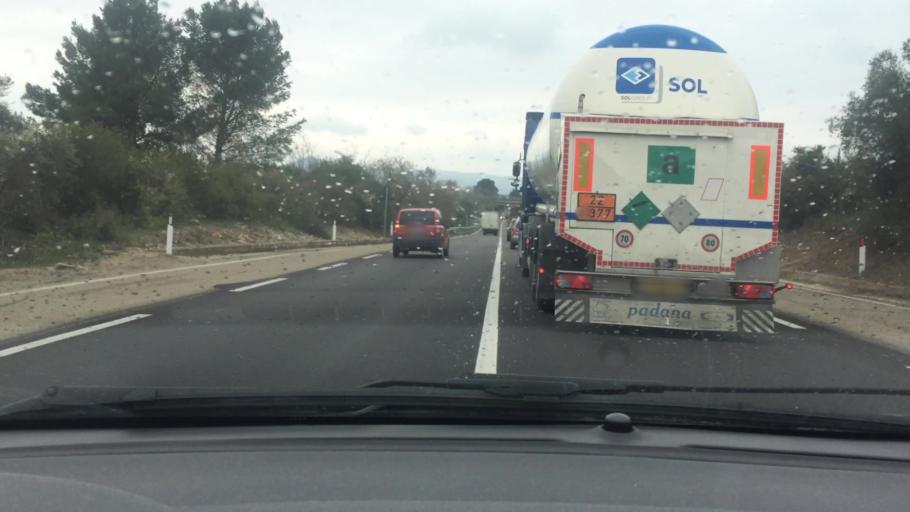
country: IT
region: Basilicate
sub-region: Provincia di Matera
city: Matera
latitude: 40.6135
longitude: 16.5763
